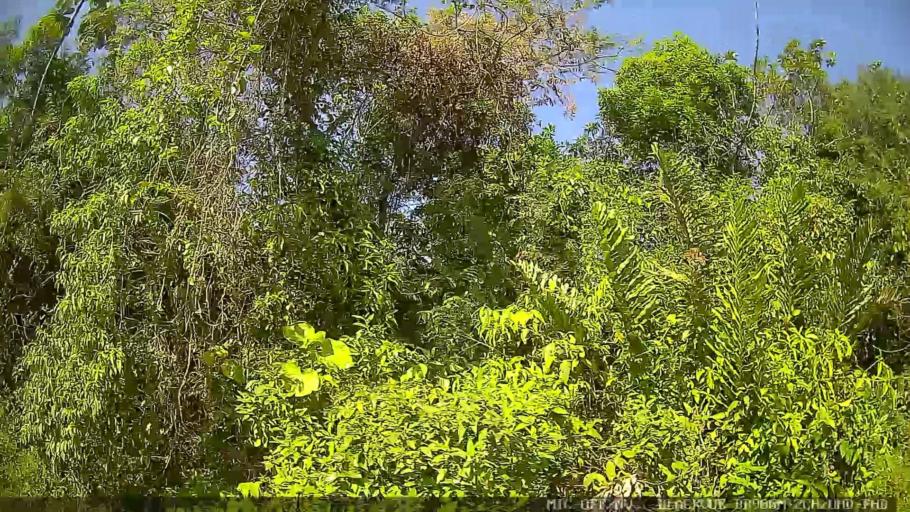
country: BR
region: Sao Paulo
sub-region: Guaruja
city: Guaruja
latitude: -24.0067
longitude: -46.2939
